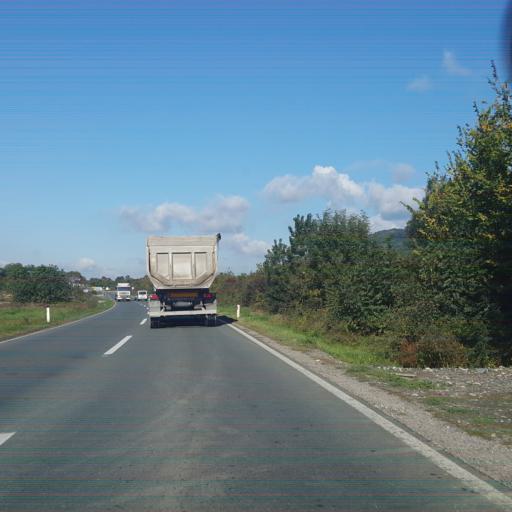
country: RS
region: Central Serbia
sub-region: Rasinski Okrug
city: Trstenik
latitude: 43.6296
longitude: 20.9700
